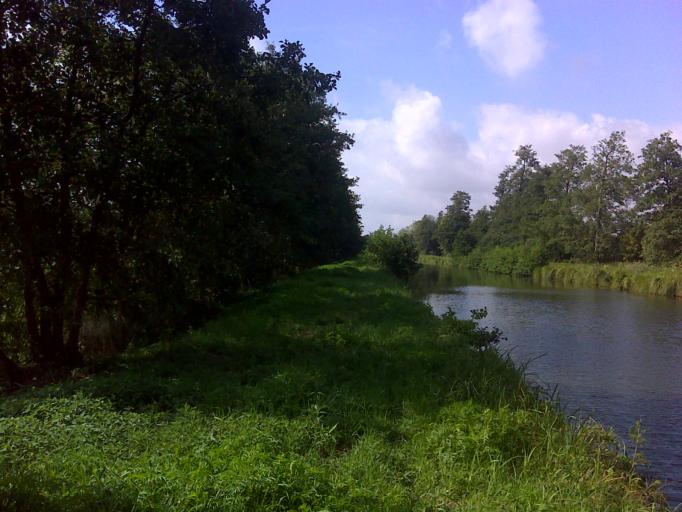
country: FR
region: Nord-Pas-de-Calais
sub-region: Departement du Nord
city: Landrecies
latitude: 50.1087
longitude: 3.6458
